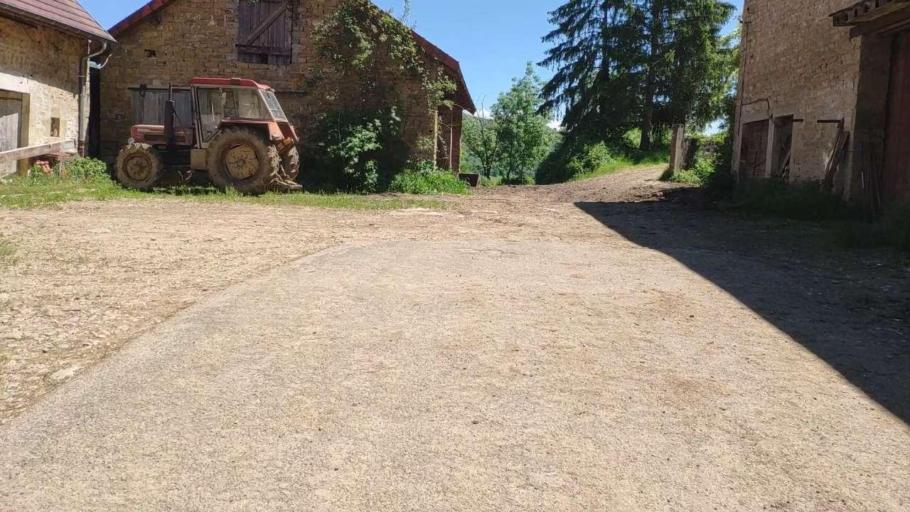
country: FR
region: Franche-Comte
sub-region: Departement du Jura
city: Perrigny
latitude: 46.7306
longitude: 5.6297
